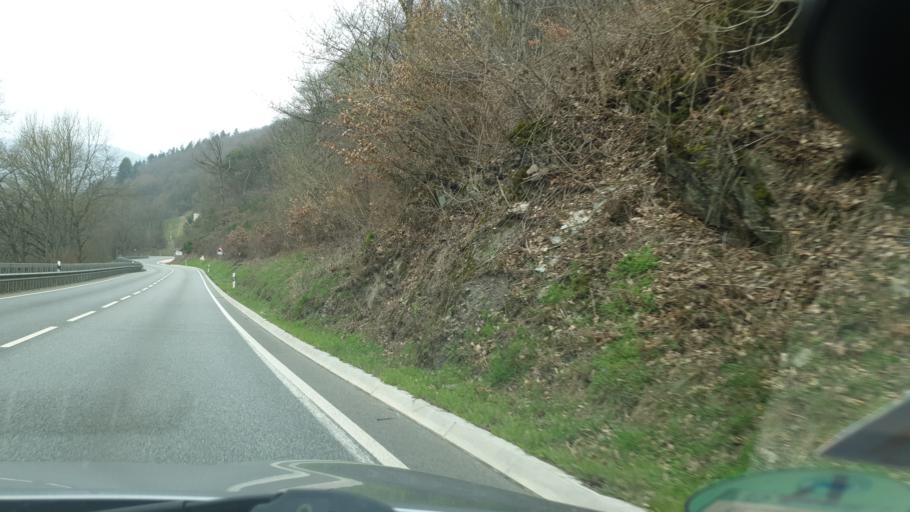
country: DE
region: Rheinland-Pfalz
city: Nassau
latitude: 50.3002
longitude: 7.8018
